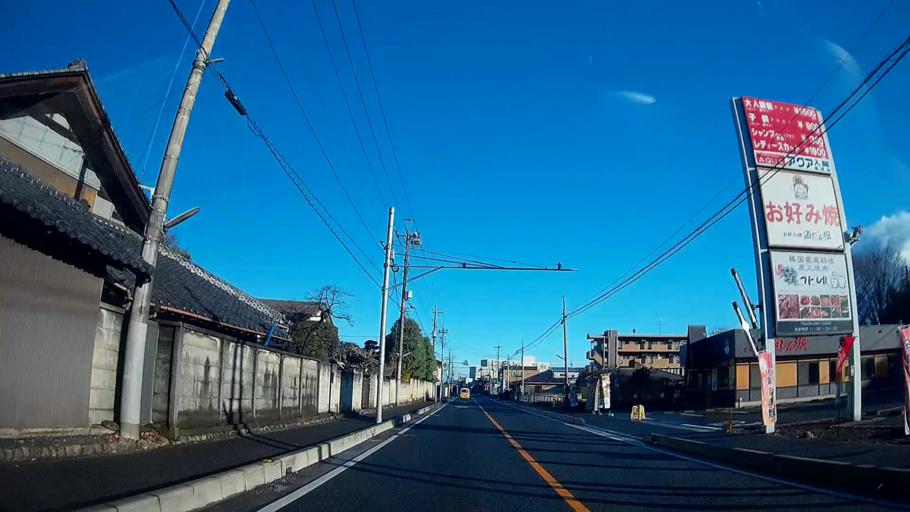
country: JP
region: Saitama
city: Sayama
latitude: 35.8451
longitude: 139.3832
